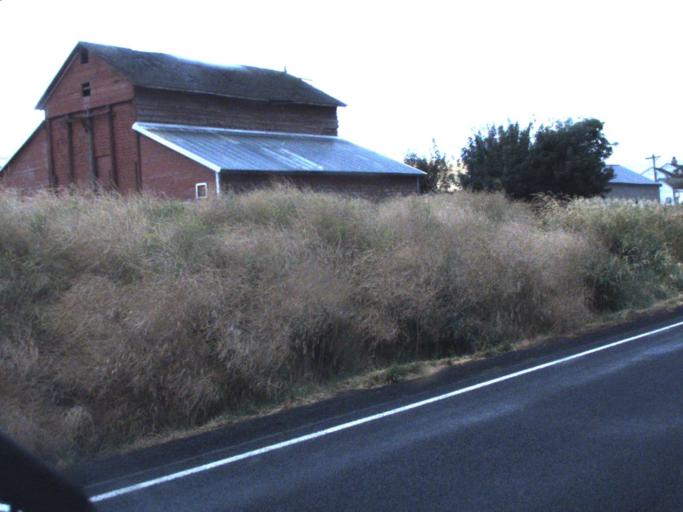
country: US
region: Washington
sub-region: Whitman County
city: Colfax
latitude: 47.0444
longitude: -117.5144
